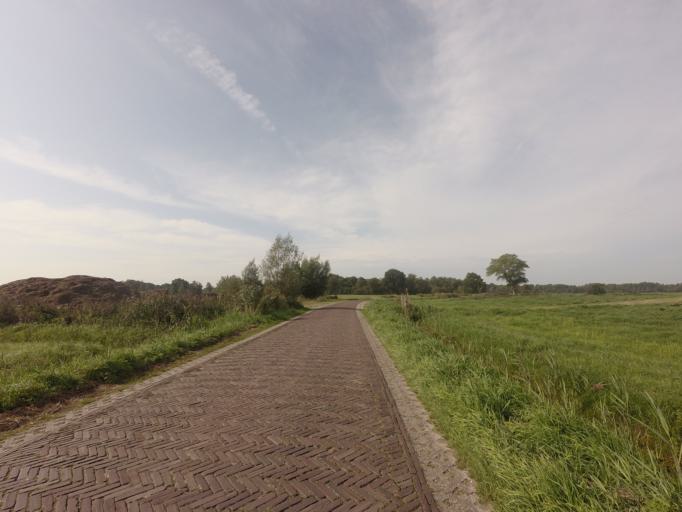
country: NL
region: Groningen
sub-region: Gemeente Leek
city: Leek
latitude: 53.1712
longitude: 6.4129
